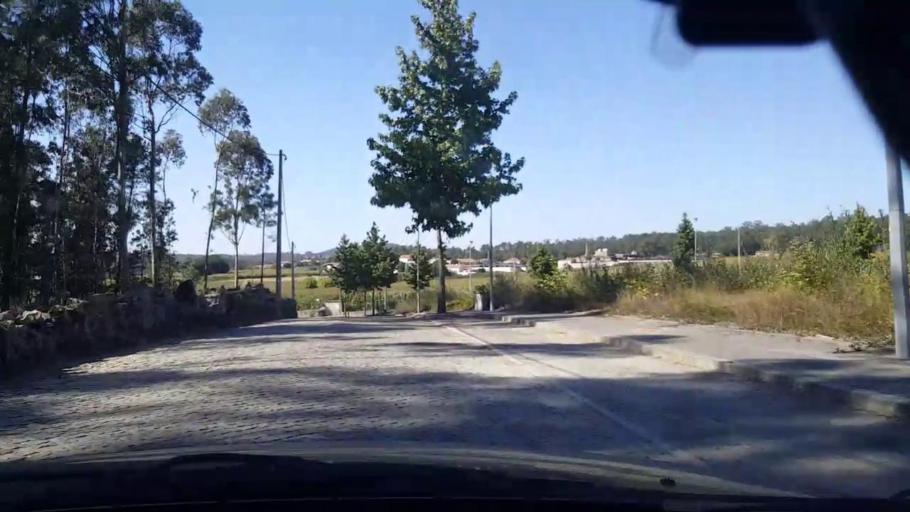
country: PT
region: Braga
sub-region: Vila Nova de Famalicao
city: Ribeirao
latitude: 41.3566
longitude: -8.6326
